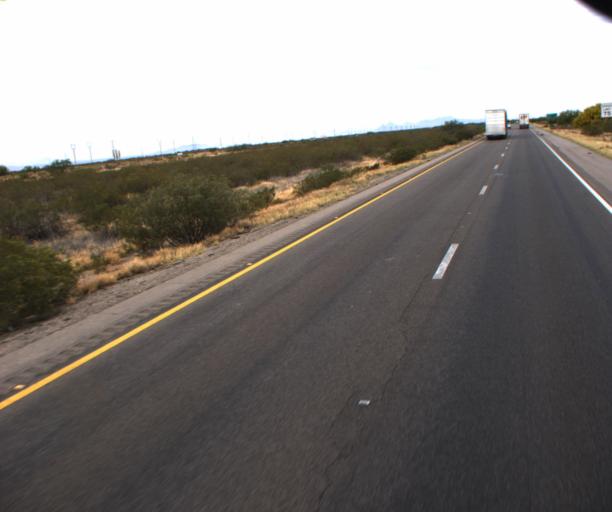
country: US
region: Arizona
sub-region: Pima County
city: Vail
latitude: 32.0355
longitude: -110.7302
